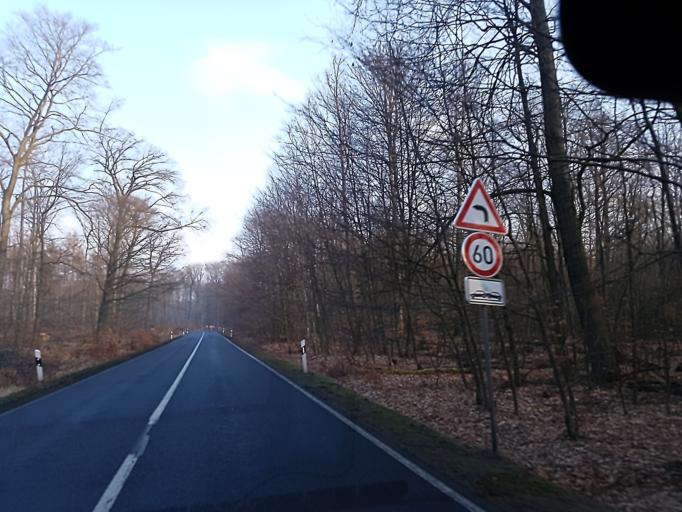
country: DE
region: Brandenburg
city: Wiesenburg
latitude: 52.0241
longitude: 12.4605
